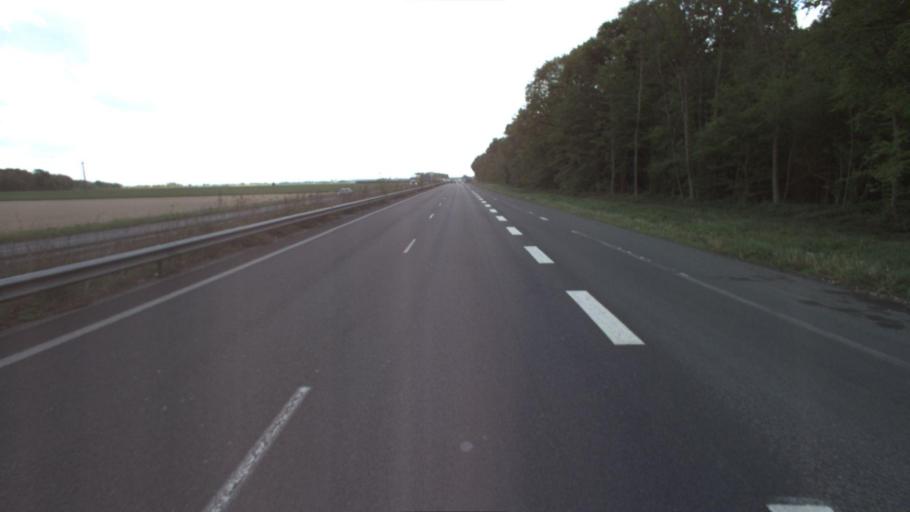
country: FR
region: Ile-de-France
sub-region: Departement de Seine-et-Marne
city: Fontenay-Tresigny
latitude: 48.6953
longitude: 2.9056
